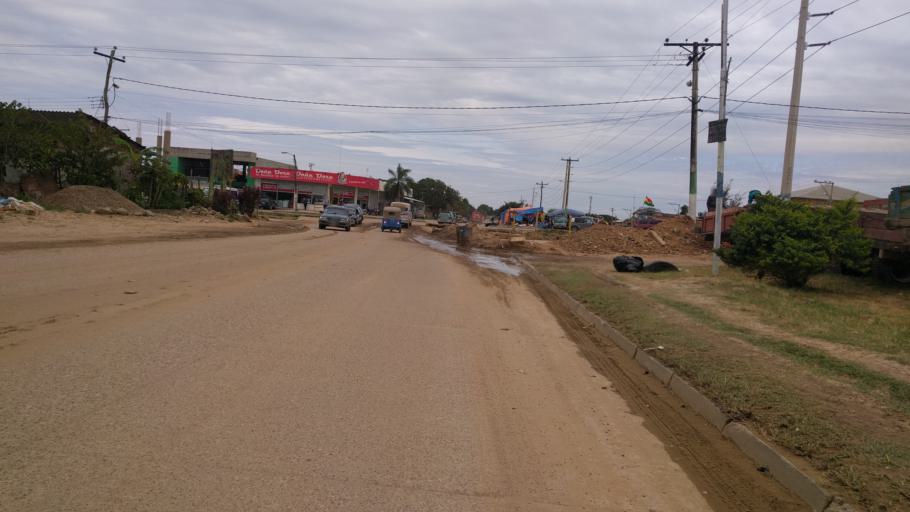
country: BO
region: Santa Cruz
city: Santa Cruz de la Sierra
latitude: -17.8518
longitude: -63.1808
